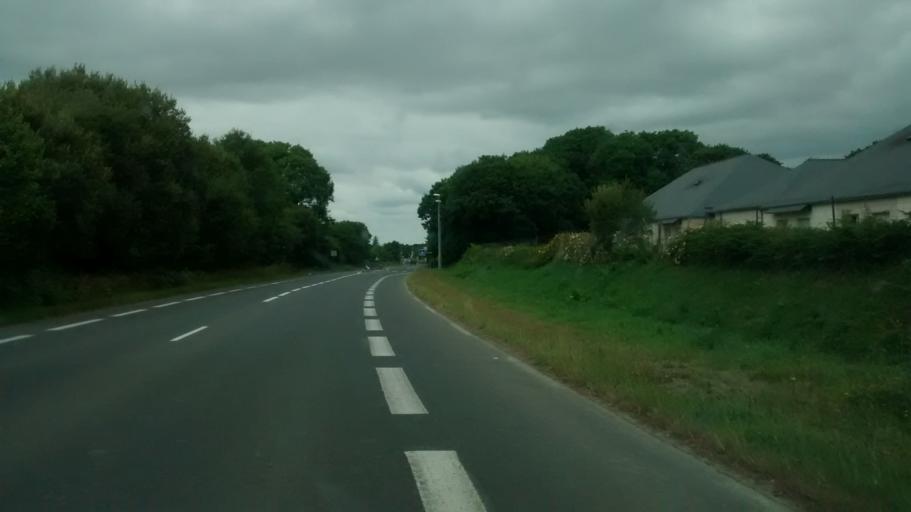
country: FR
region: Brittany
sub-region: Departement du Finistere
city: Plougastel-Daoulas
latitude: 48.3776
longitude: -4.3796
